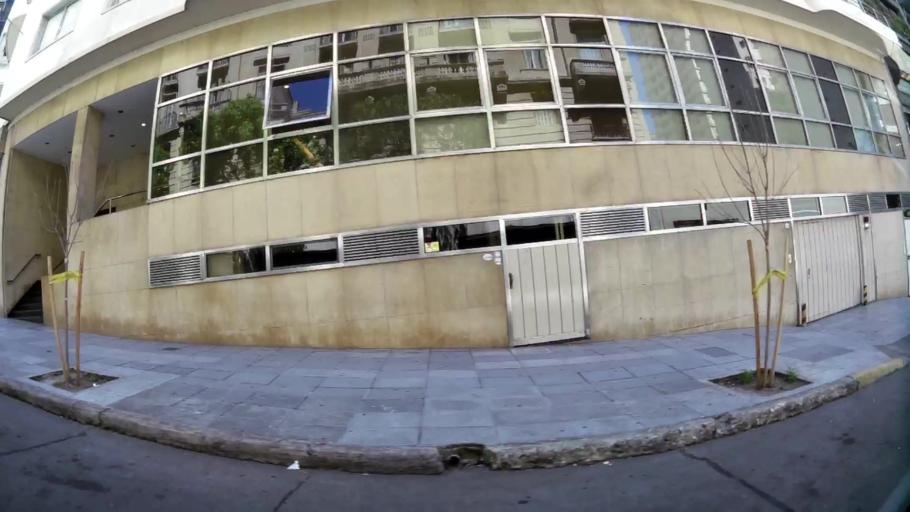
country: AR
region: Buenos Aires F.D.
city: Retiro
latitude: -34.5921
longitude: -58.3785
